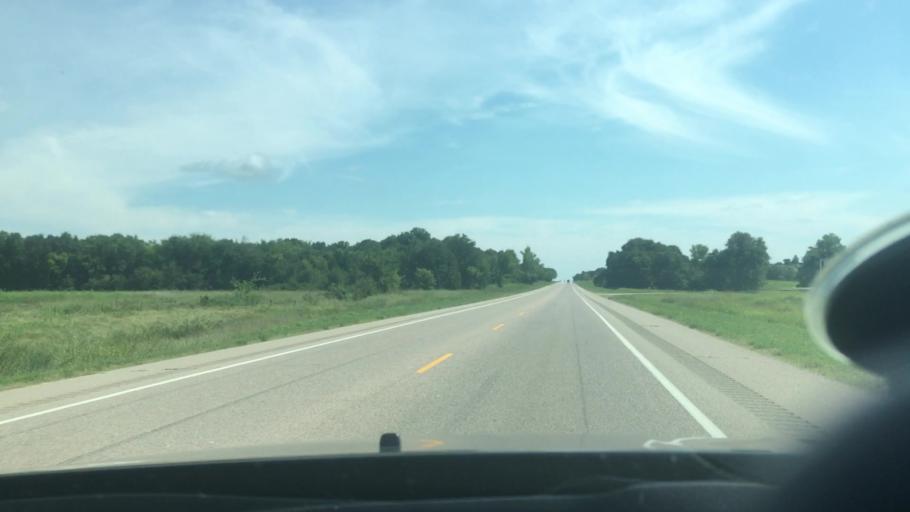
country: US
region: Oklahoma
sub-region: Seminole County
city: Seminole
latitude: 35.1685
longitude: -96.6742
